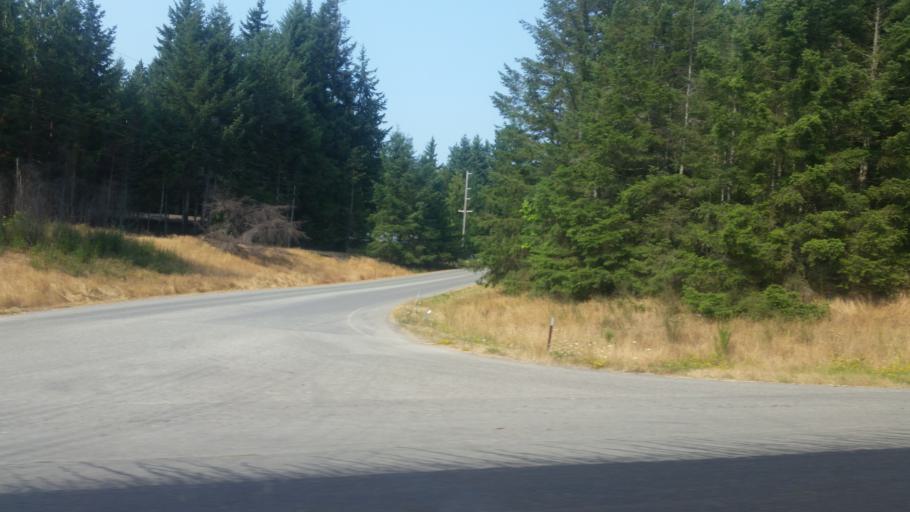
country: US
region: Washington
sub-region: Clallam County
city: Port Angeles
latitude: 48.0996
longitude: -123.5536
